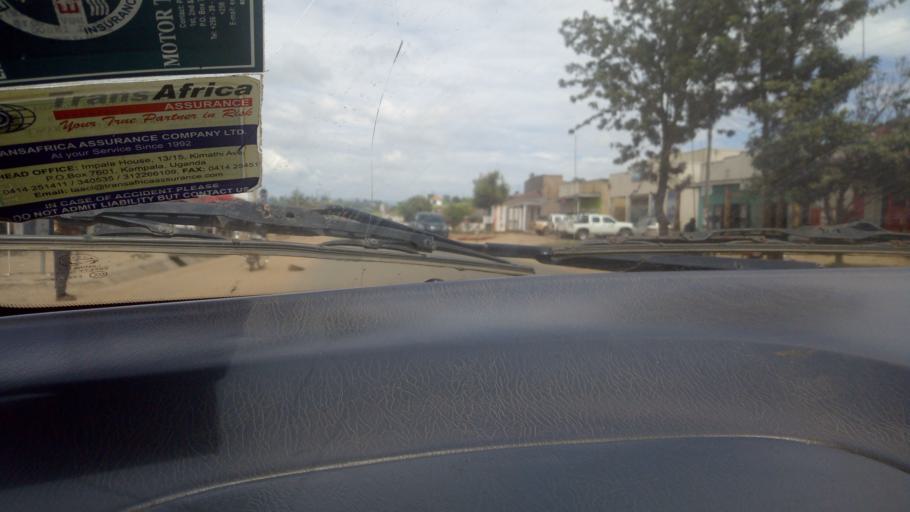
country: UG
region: Western Region
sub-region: Mbarara District
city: Bwizibwera
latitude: -0.4359
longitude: 30.5727
